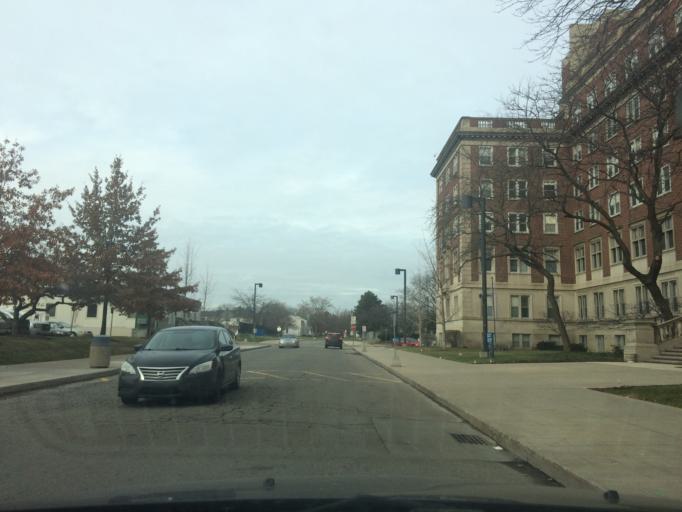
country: US
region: Michigan
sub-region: Wayne County
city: Highland Park
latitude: 42.3676
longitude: -83.0866
